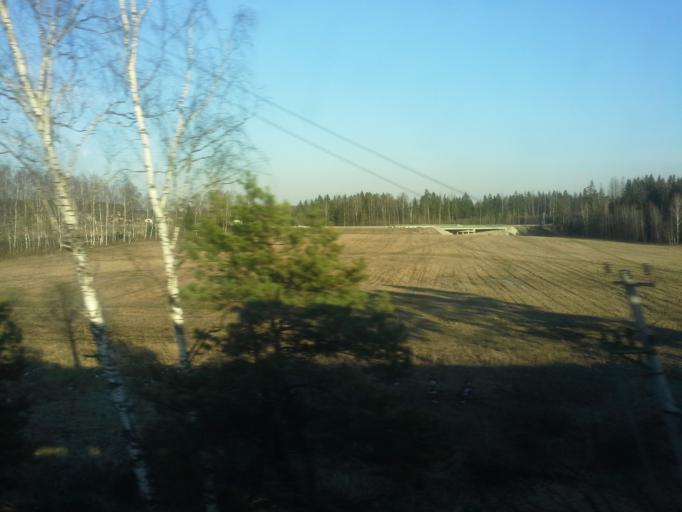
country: RU
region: Moskovskaya
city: Nekrasovskiy
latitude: 56.1049
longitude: 37.5134
